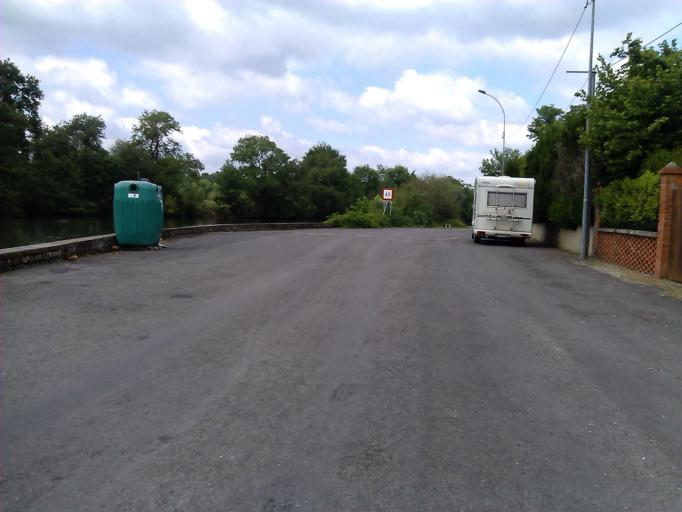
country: FR
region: Poitou-Charentes
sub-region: Departement de la Charente
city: Angouleme
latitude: 45.6557
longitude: 0.1463
